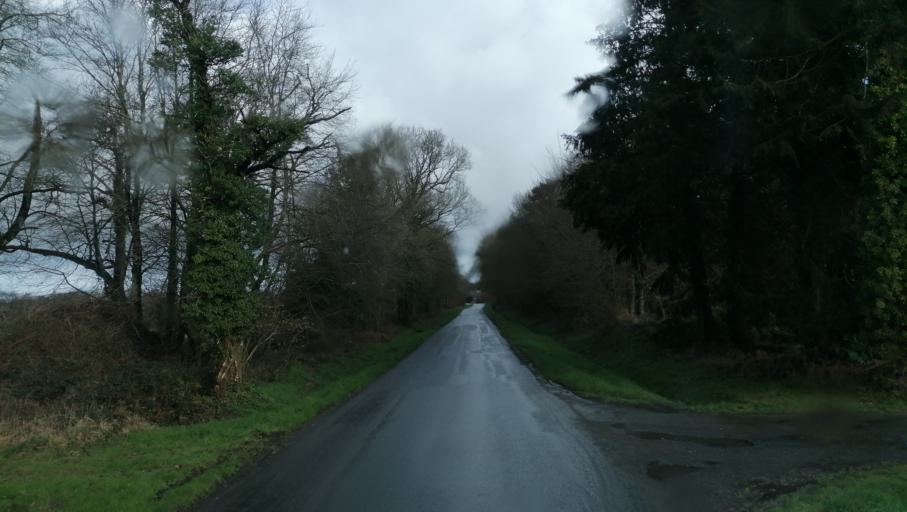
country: FR
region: Brittany
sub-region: Departement des Cotes-d'Armor
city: Lanrodec
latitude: 48.5033
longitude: -3.0293
